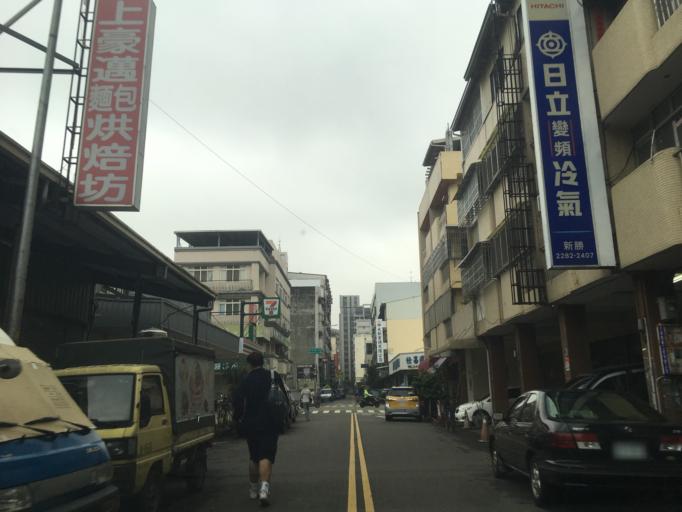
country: TW
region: Taiwan
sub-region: Taichung City
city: Taichung
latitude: 24.1730
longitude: 120.6939
